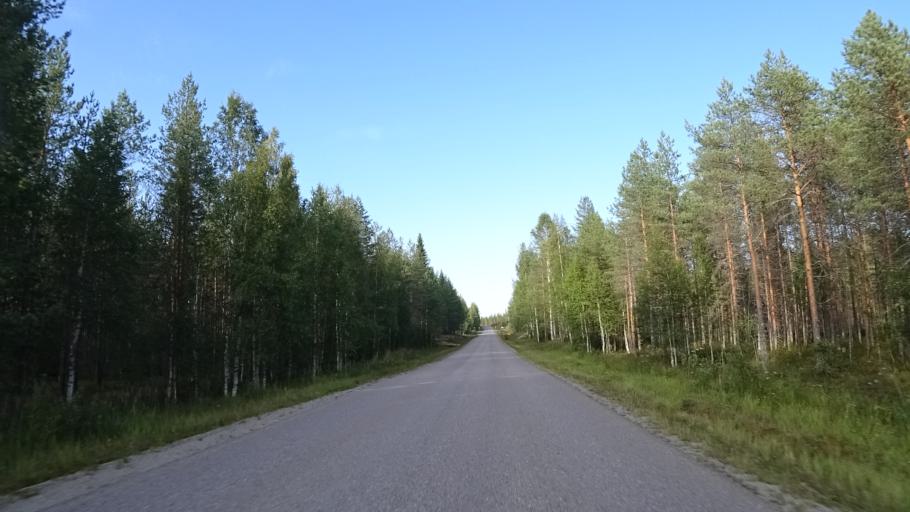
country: FI
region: North Karelia
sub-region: Joensuu
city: Eno
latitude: 63.0627
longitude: 30.5510
